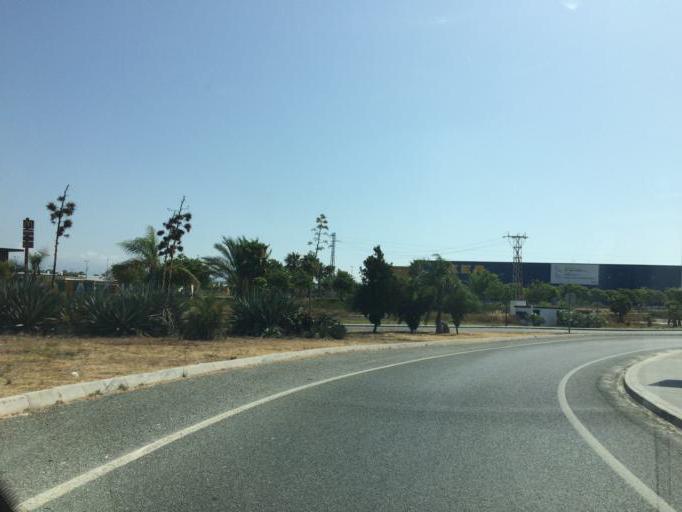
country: ES
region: Andalusia
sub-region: Provincia de Malaga
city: Torremolinos
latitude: 36.6571
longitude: -4.4856
